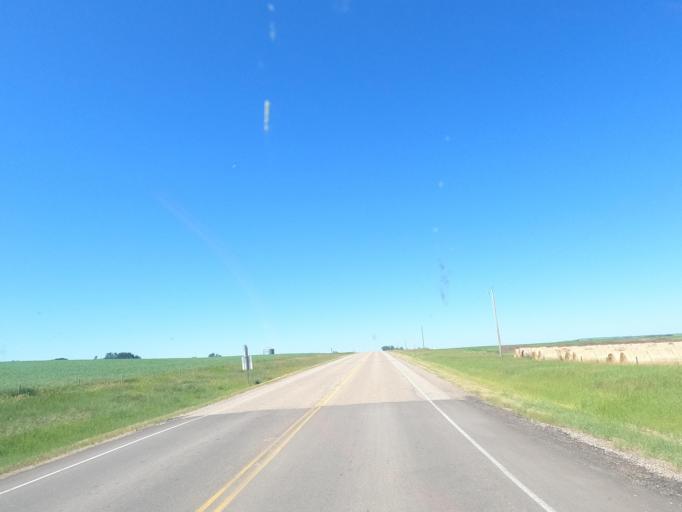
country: CA
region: Alberta
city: Strathmore
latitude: 51.1543
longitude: -113.2623
